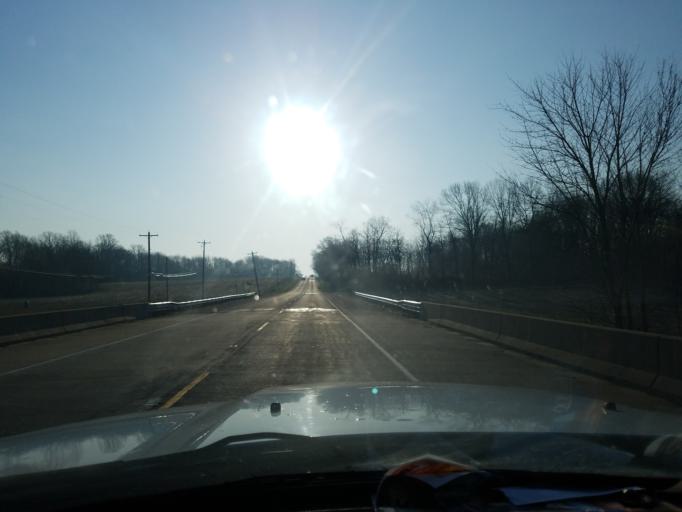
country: US
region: Indiana
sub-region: Vigo County
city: Seelyville
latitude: 39.3899
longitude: -87.2304
